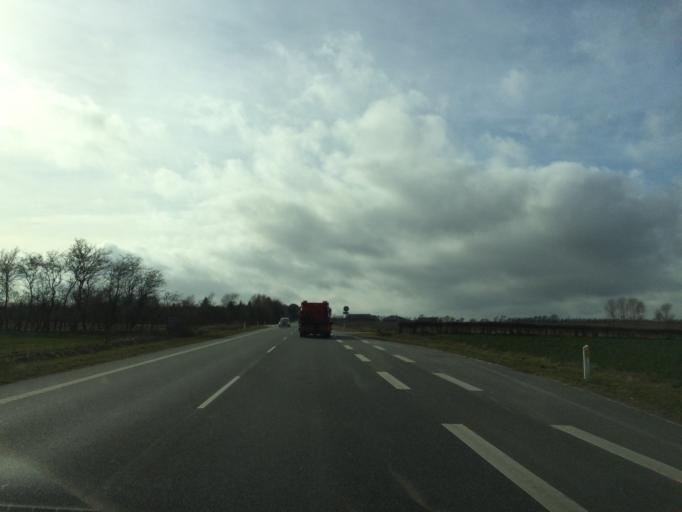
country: DK
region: Central Jutland
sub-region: Randers Kommune
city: Langa
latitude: 56.4745
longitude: 9.9331
